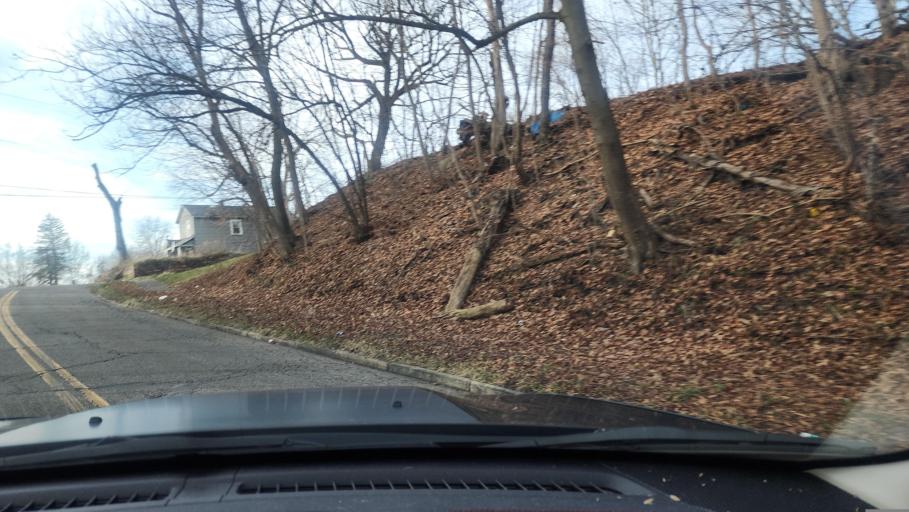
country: US
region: Ohio
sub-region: Mahoning County
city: Youngstown
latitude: 41.1022
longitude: -80.6249
